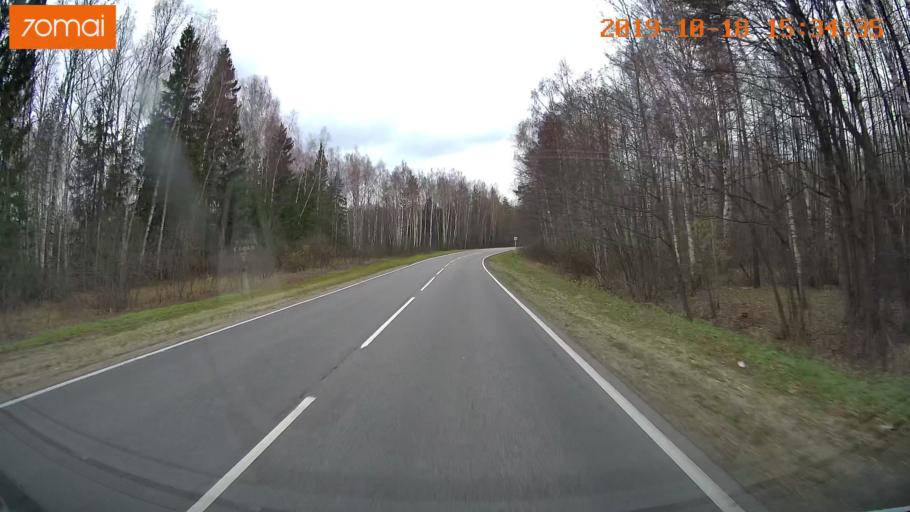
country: RU
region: Vladimir
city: Anopino
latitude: 55.8559
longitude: 40.6404
